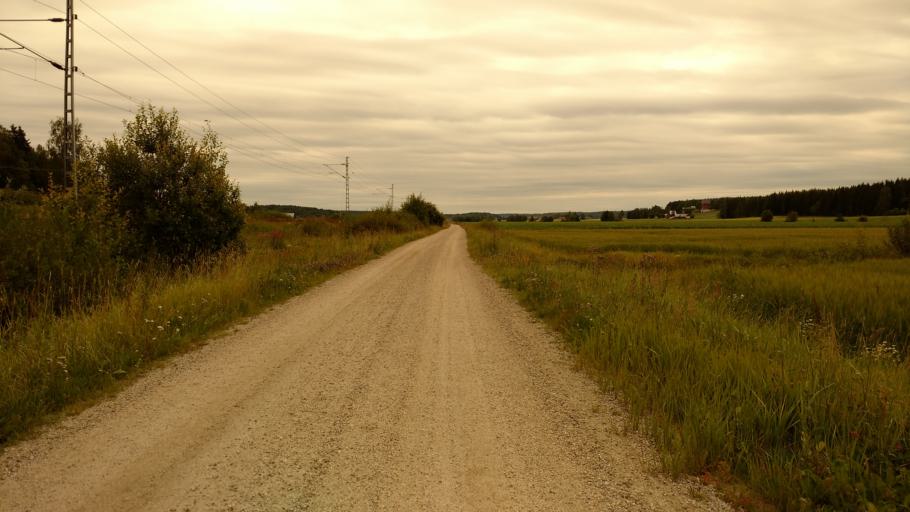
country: FI
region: Varsinais-Suomi
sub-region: Turku
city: Paimio
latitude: 60.4233
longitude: 22.8141
